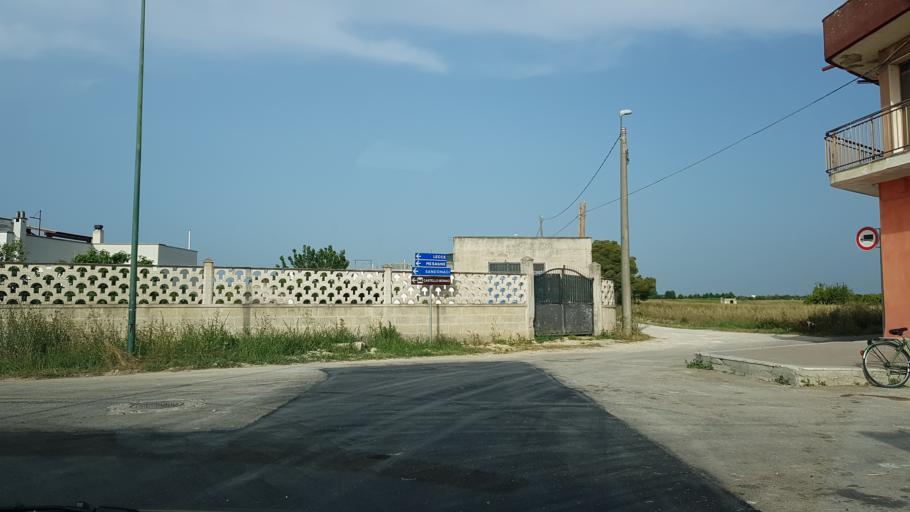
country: IT
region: Apulia
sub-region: Provincia di Brindisi
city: San Pancrazio Salentino
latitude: 40.4145
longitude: 17.8447
